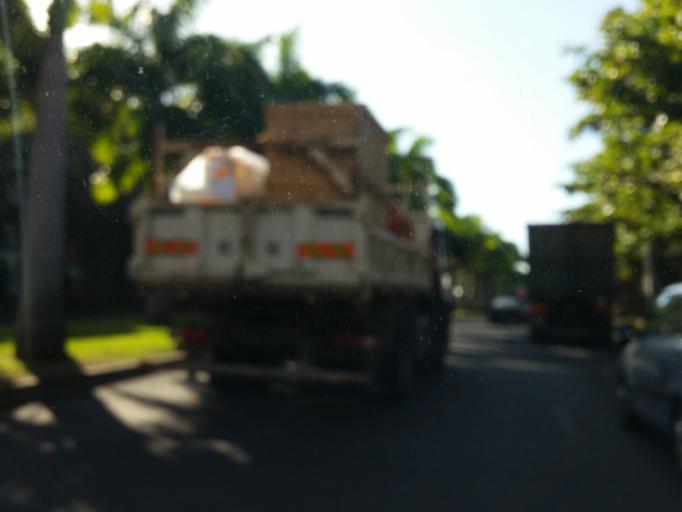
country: RE
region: Reunion
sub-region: Reunion
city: Saint-Denis
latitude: -20.8900
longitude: 55.4616
